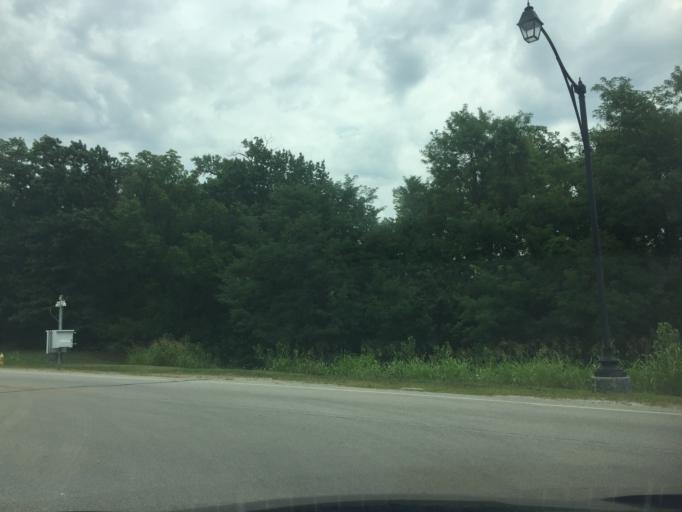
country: US
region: Kansas
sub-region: Leavenworth County
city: Leavenworth
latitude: 39.3361
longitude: -94.9155
